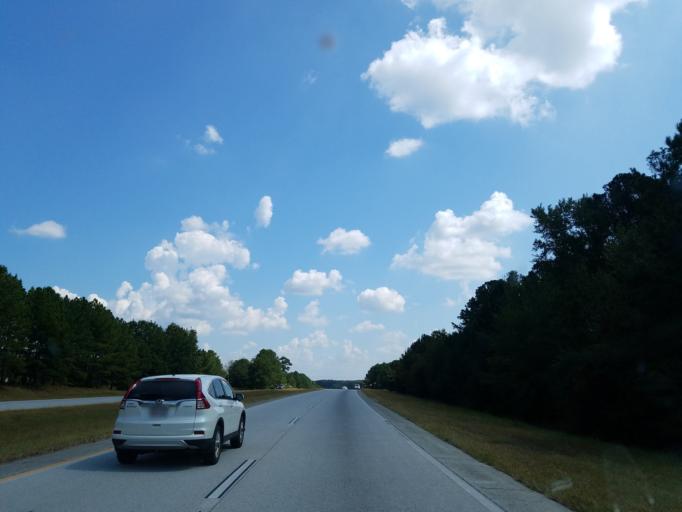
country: US
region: Georgia
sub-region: Barrow County
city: Statham
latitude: 33.9519
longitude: -83.5931
